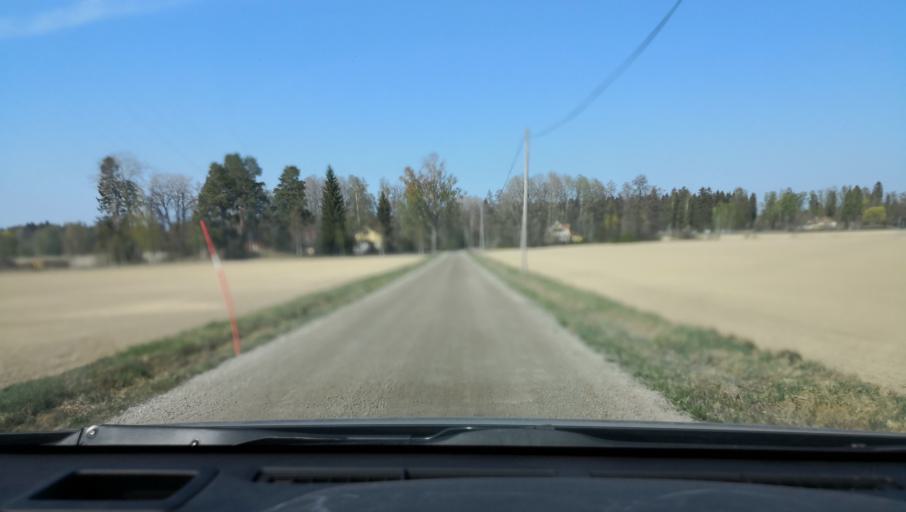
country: SE
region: Uppsala
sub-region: Heby Kommun
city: Heby
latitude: 60.0326
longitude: 16.7823
